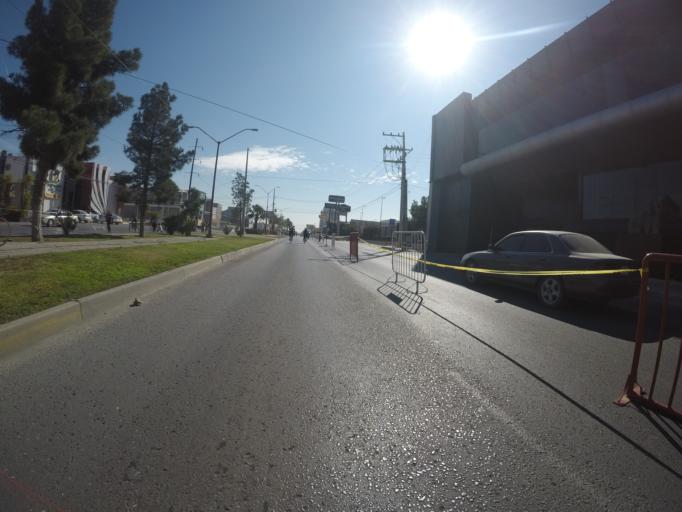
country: MX
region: Chihuahua
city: Ciudad Juarez
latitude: 31.7314
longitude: -106.4116
